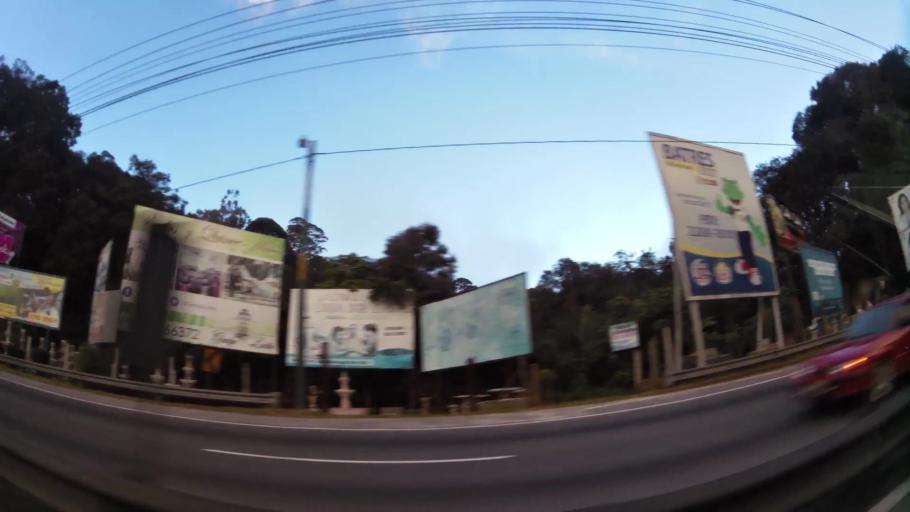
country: GT
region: Sacatepequez
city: San Lucas Sacatepequez
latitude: 14.6126
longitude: -90.6505
